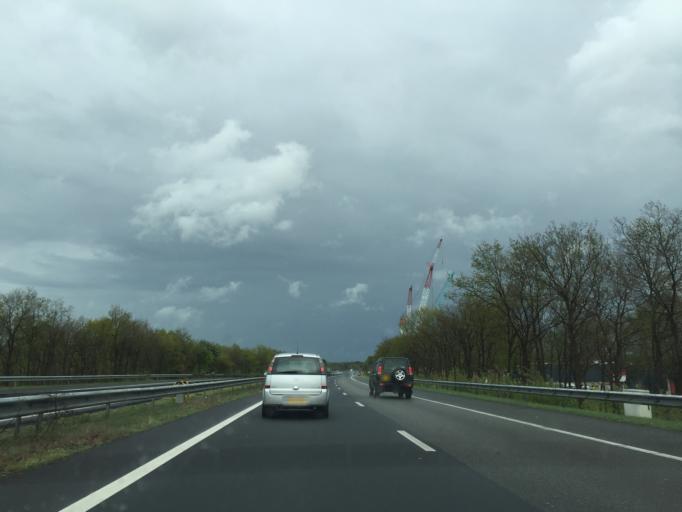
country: NL
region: Gelderland
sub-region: Gemeente Oldebroek
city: Oldebroek
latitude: 52.4103
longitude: 5.8903
